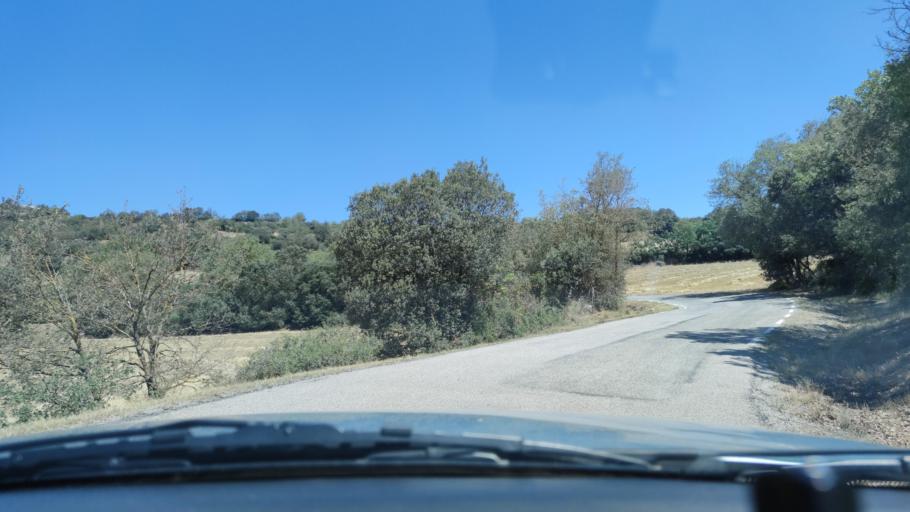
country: ES
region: Catalonia
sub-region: Provincia de Lleida
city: Tora de Riubregos
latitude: 41.8793
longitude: 1.4380
